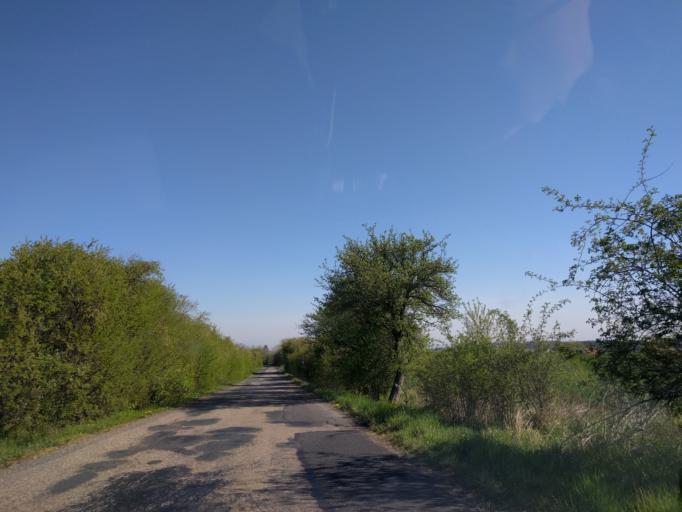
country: CZ
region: Central Bohemia
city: Mukarov
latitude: 49.9992
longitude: 14.7758
